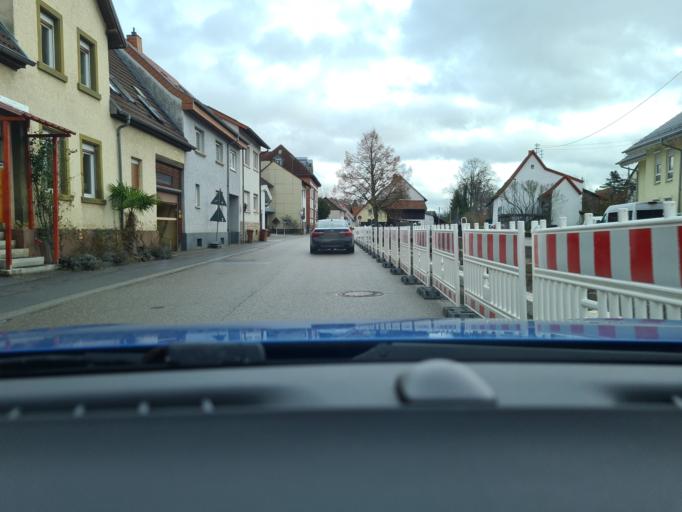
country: DE
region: Baden-Wuerttemberg
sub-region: Karlsruhe Region
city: Dielheim
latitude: 49.3012
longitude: 8.7415
